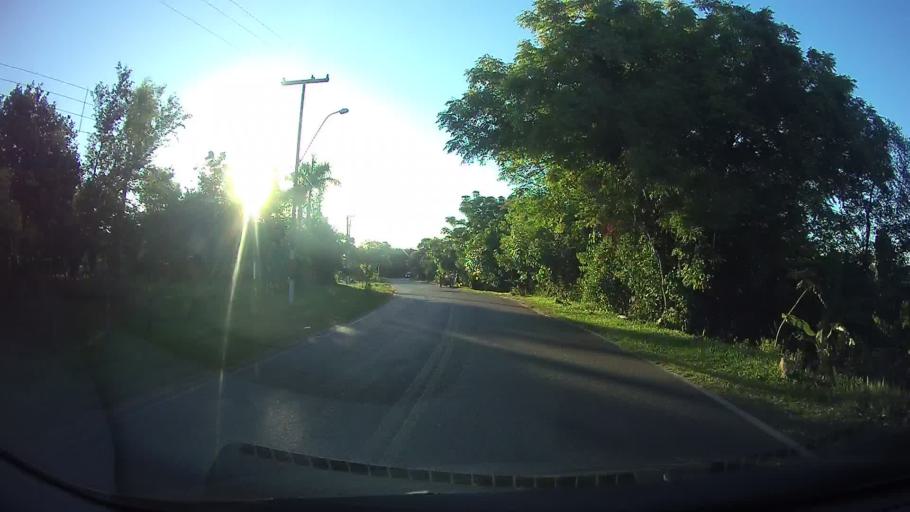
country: PY
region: Central
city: Aregua
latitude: -25.2631
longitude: -57.4184
